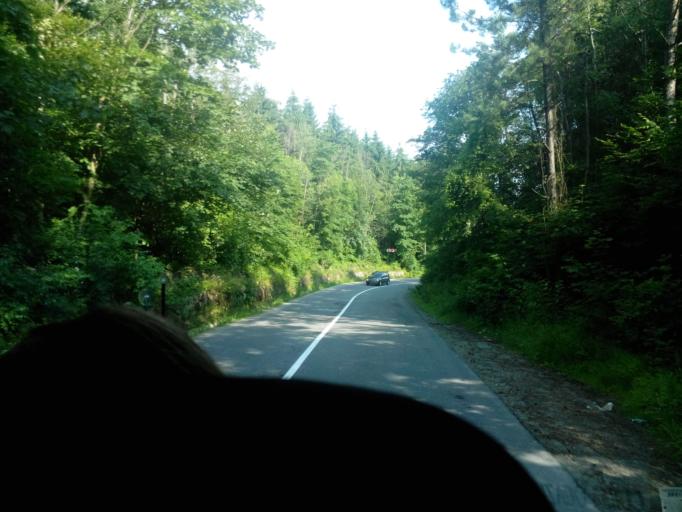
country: RO
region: Brasov
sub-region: Oras Predeal
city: Predeal
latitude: 45.5186
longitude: 25.5078
